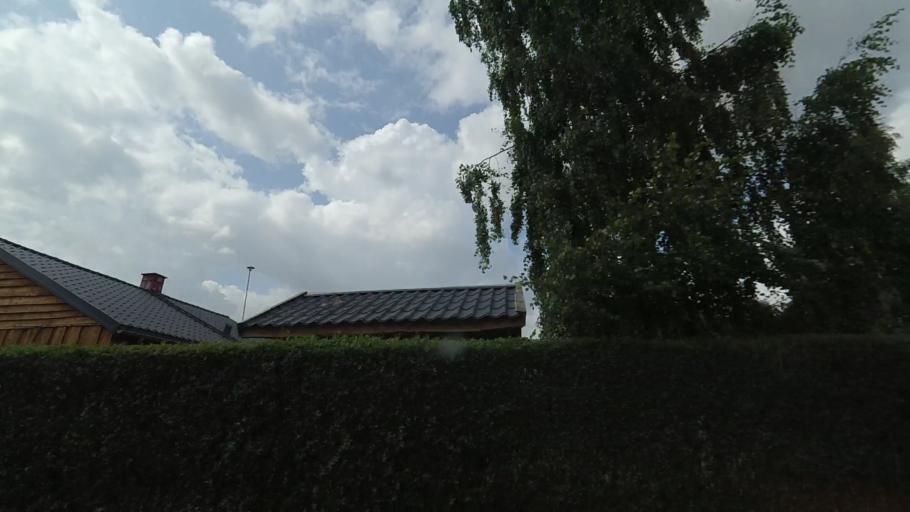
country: DK
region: Central Jutland
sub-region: Norddjurs Kommune
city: Allingabro
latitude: 56.5388
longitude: 10.3632
